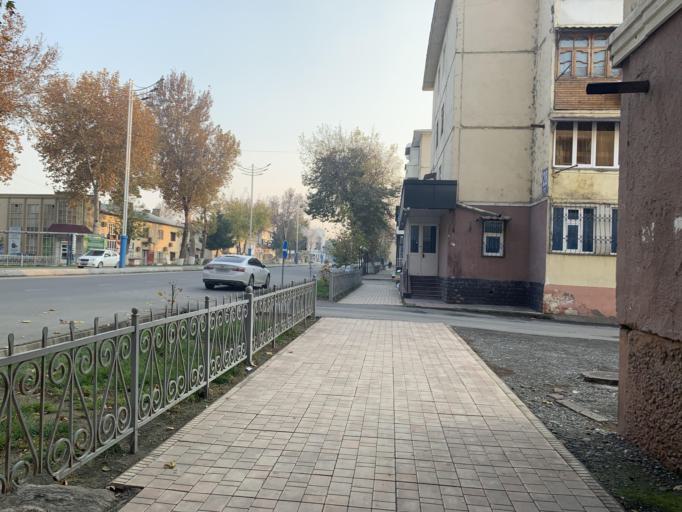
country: UZ
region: Fergana
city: Qo`qon
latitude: 40.5288
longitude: 70.9390
